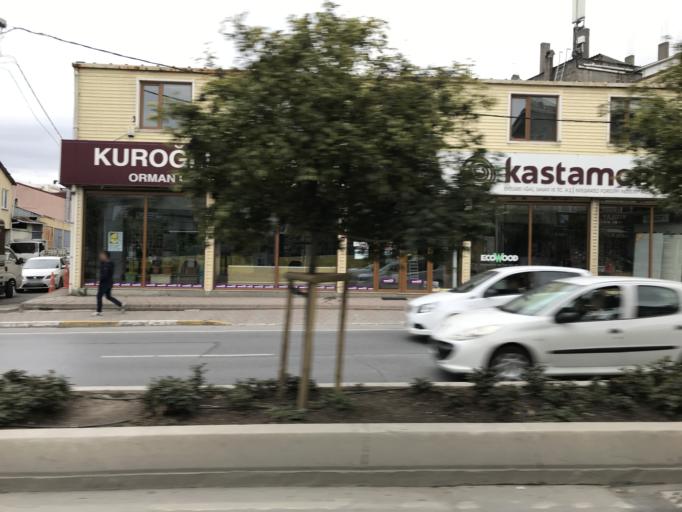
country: TR
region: Istanbul
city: Umraniye
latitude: 41.0084
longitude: 29.1628
